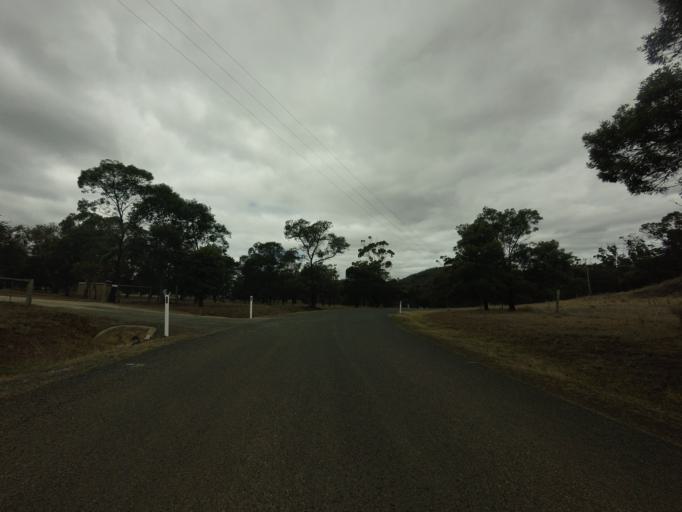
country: AU
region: Tasmania
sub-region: Clarence
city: Cambridge
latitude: -42.7906
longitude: 147.4024
